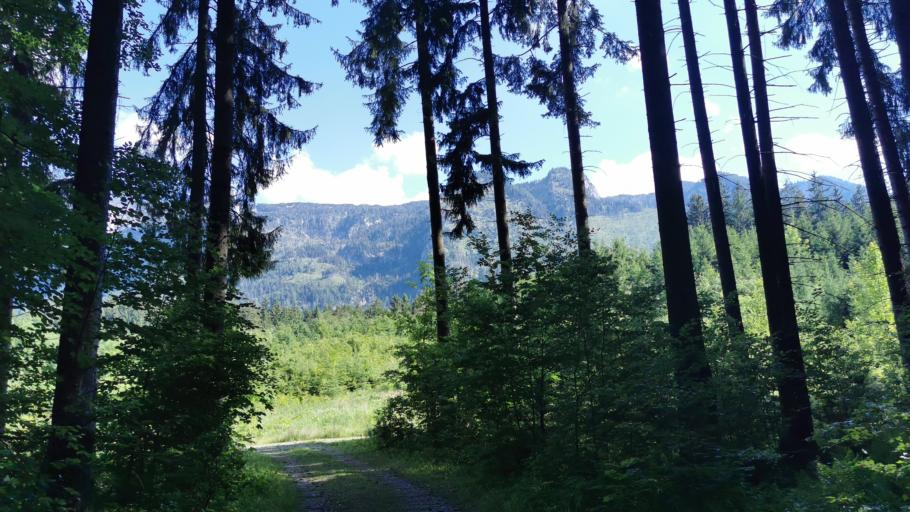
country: DE
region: Bavaria
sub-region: Upper Bavaria
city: Piding
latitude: 47.7440
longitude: 12.9680
